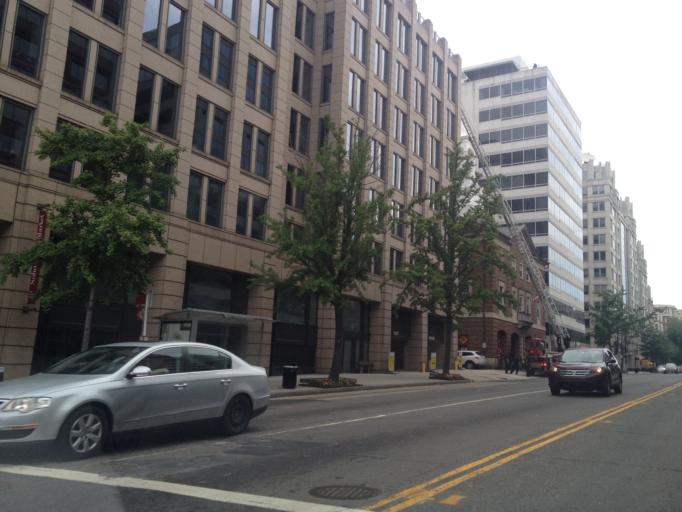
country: US
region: Washington, D.C.
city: Washington, D.C.
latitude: 38.9027
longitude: -77.0296
